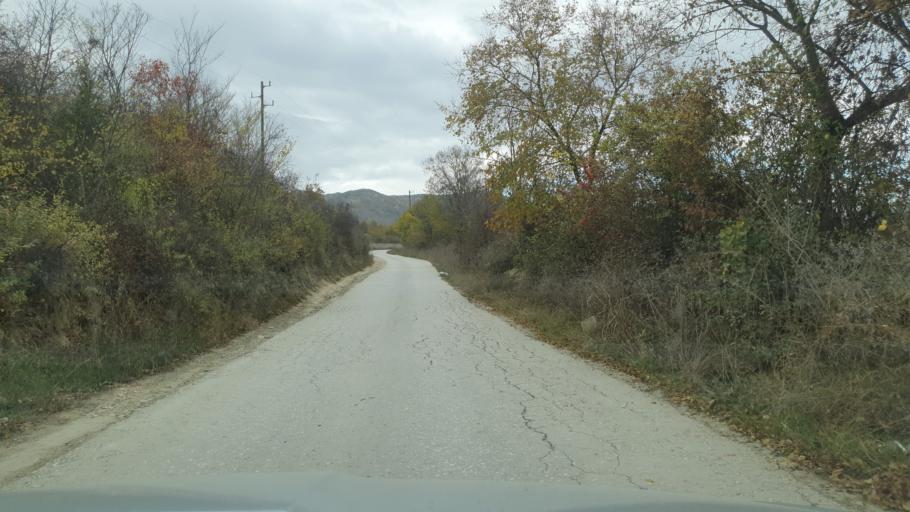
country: MK
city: Kondovo
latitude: 42.0374
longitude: 21.2812
